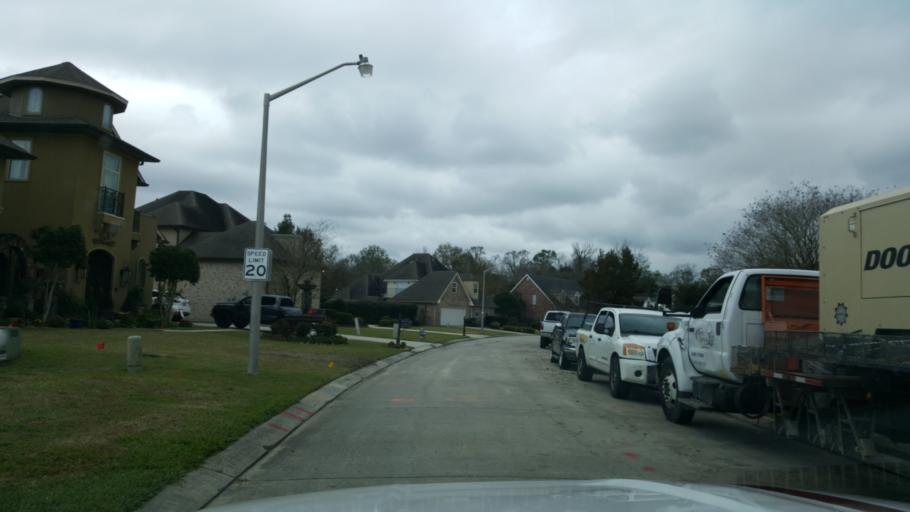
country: US
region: Louisiana
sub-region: Jefferson Parish
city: Woodmere
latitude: 29.8734
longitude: -90.0763
